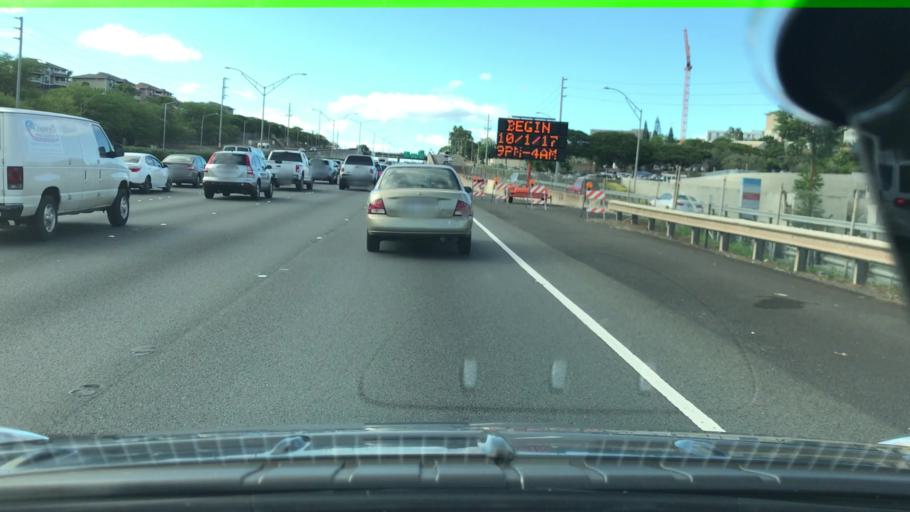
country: US
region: Hawaii
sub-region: Honolulu County
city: Halawa Heights
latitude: 21.3623
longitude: -157.9004
